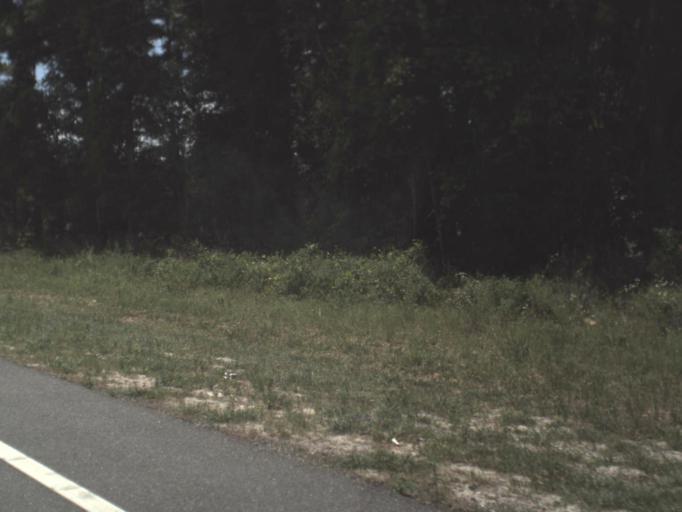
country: US
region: Florida
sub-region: Dixie County
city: Cross City
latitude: 29.7163
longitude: -82.9845
